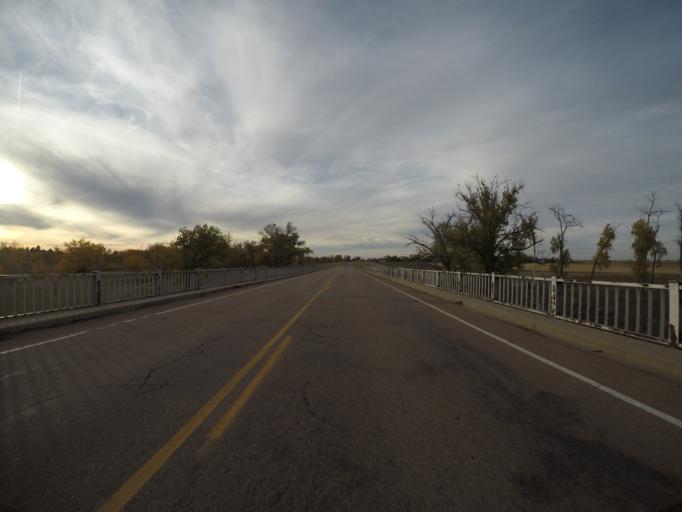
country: US
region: Colorado
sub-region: Yuma County
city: Yuma
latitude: 39.6575
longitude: -102.8460
